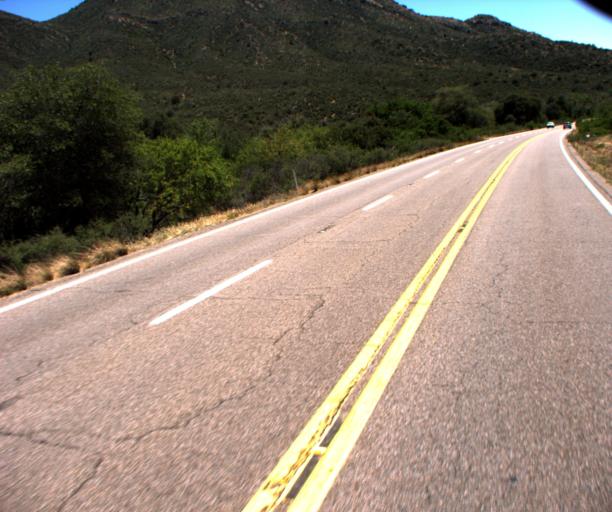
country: US
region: Arizona
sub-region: Gila County
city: Globe
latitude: 33.2280
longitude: -110.7889
